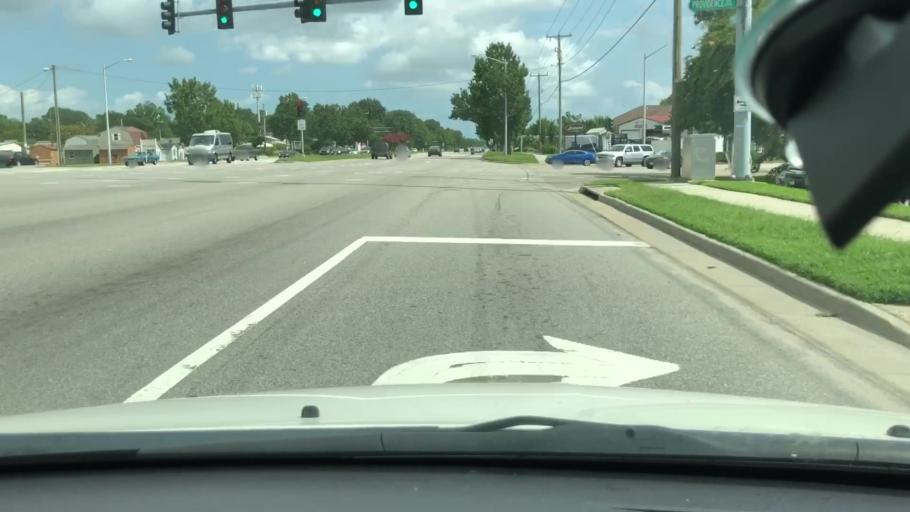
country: US
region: Virginia
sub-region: City of Chesapeake
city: Chesapeake
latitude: 36.8109
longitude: -76.2181
